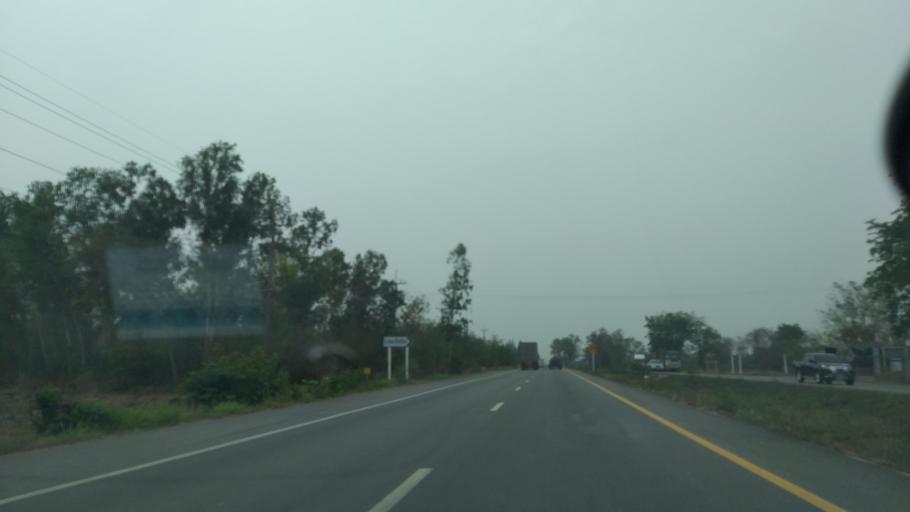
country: TH
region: Chachoengsao
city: Plaeng Yao
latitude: 13.5073
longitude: 101.2695
